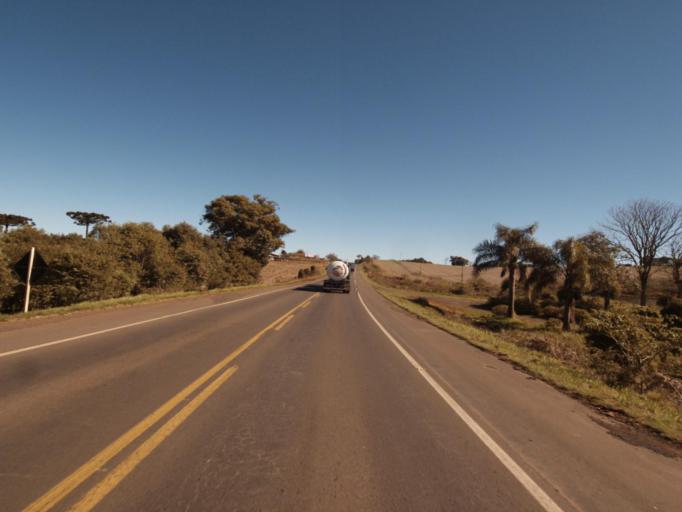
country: BR
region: Santa Catarina
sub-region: Xanxere
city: Xanxere
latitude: -26.8731
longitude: -52.3212
